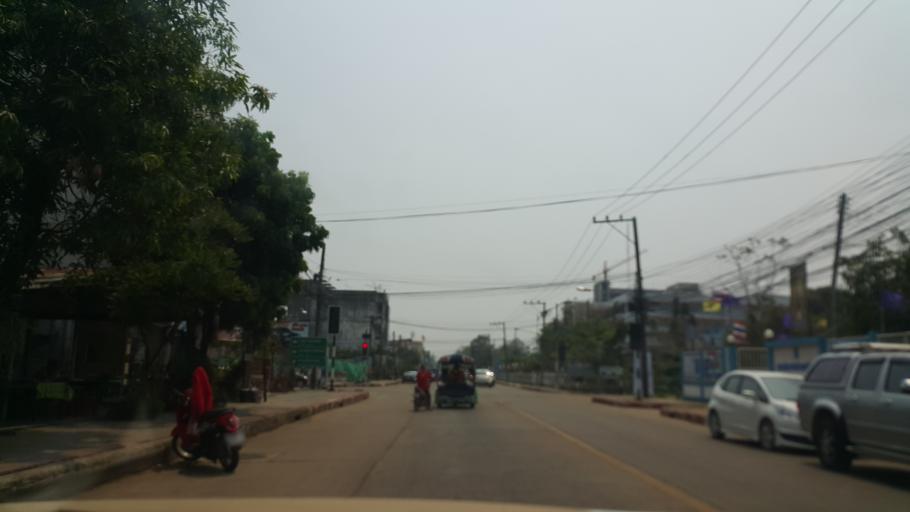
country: TH
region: Nakhon Phanom
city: Nakhon Phanom
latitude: 17.4159
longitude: 104.7773
